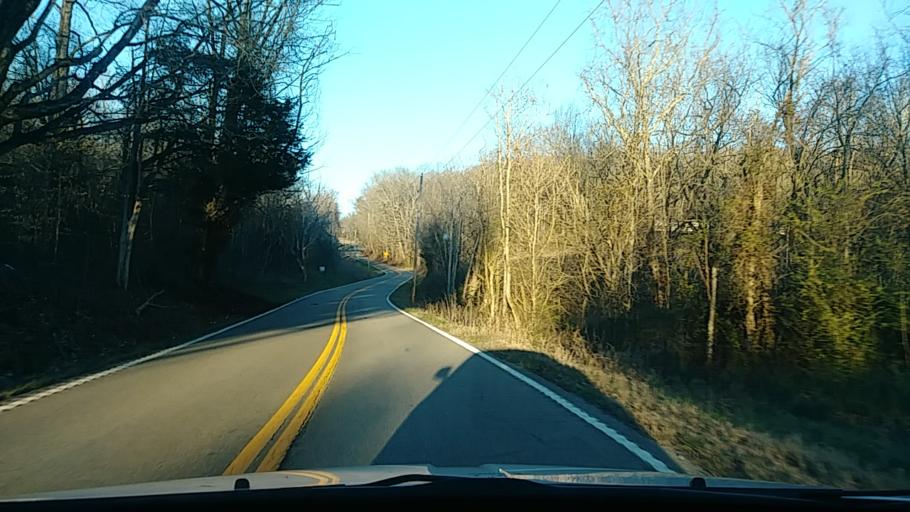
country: US
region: Tennessee
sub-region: Jefferson County
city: White Pine
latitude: 36.1238
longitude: -83.1182
